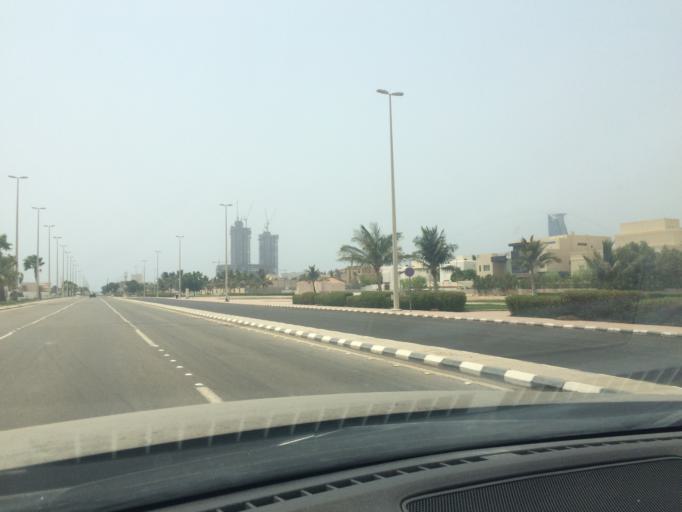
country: SA
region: Makkah
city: Jeddah
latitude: 21.5906
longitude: 39.1216
